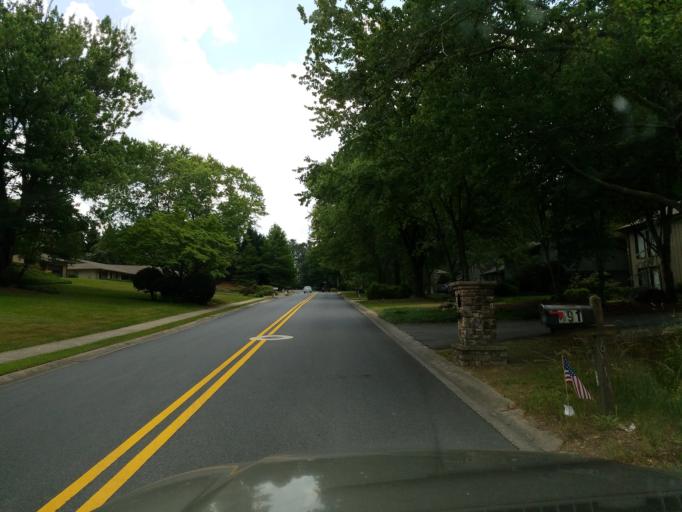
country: US
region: Georgia
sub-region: Fulton County
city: Sandy Springs
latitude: 33.9658
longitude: -84.4257
